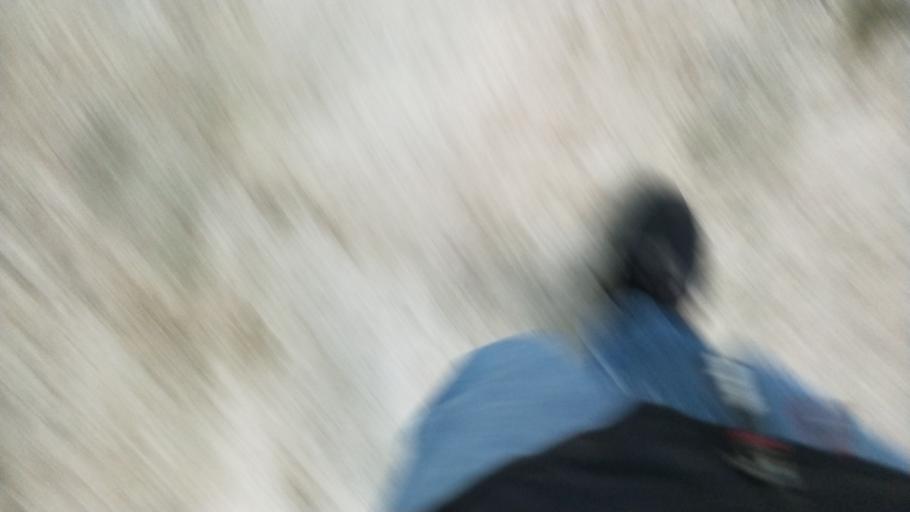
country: TW
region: Taiwan
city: Taoyuan City
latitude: 24.9729
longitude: 121.2333
